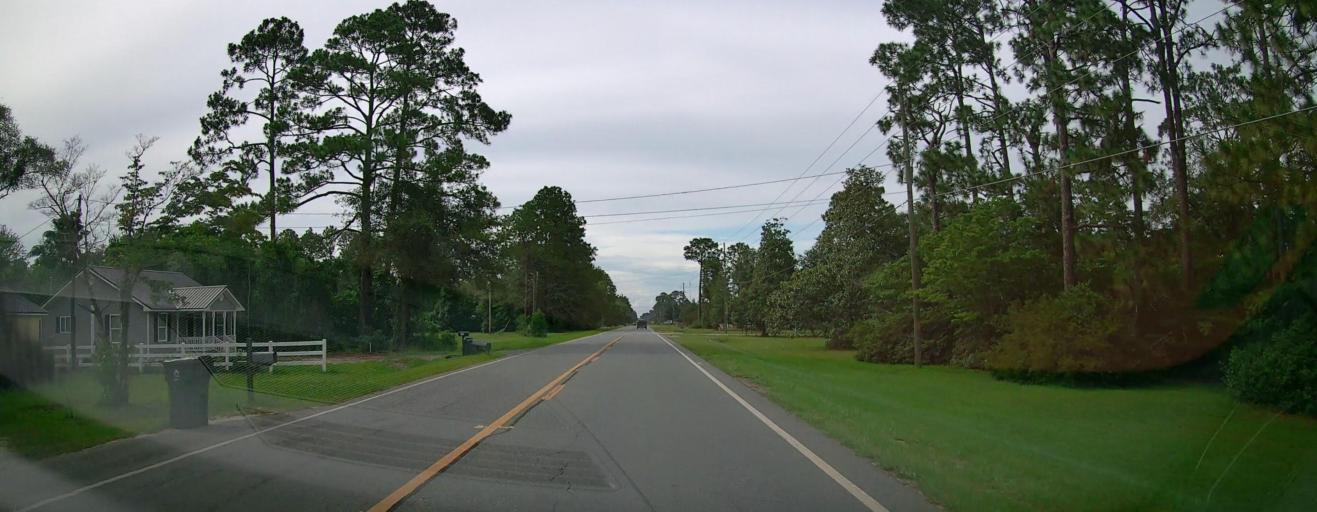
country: US
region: Georgia
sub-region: Wayne County
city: Jesup
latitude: 31.6316
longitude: -81.9016
